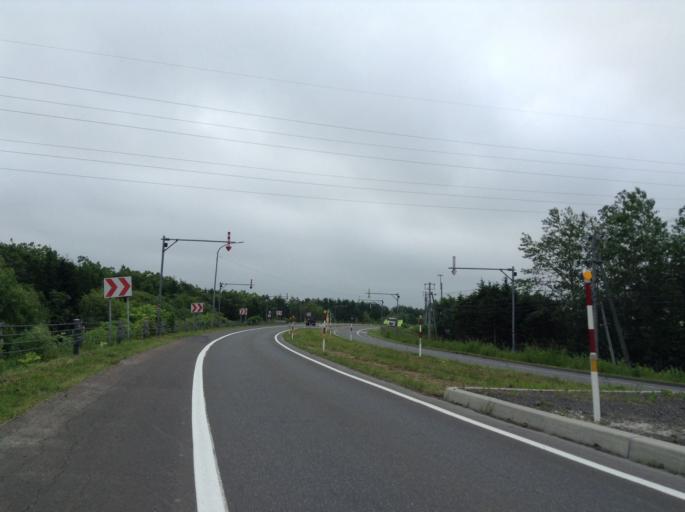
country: JP
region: Hokkaido
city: Wakkanai
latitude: 45.3693
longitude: 141.7260
